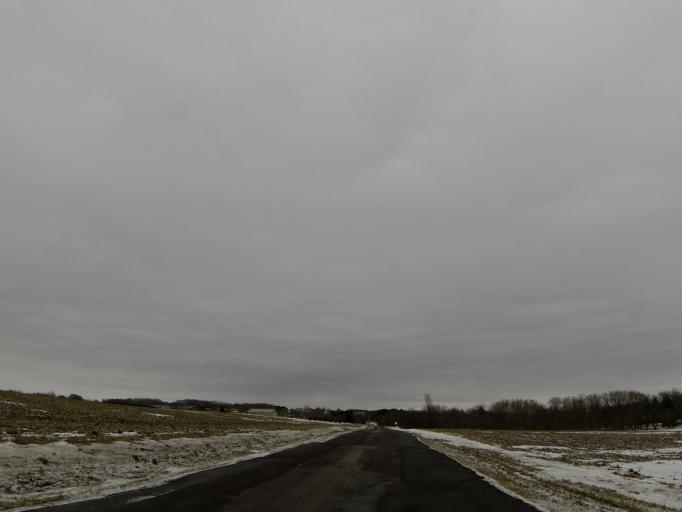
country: US
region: Minnesota
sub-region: Dakota County
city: Hastings
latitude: 44.7994
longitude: -92.8697
